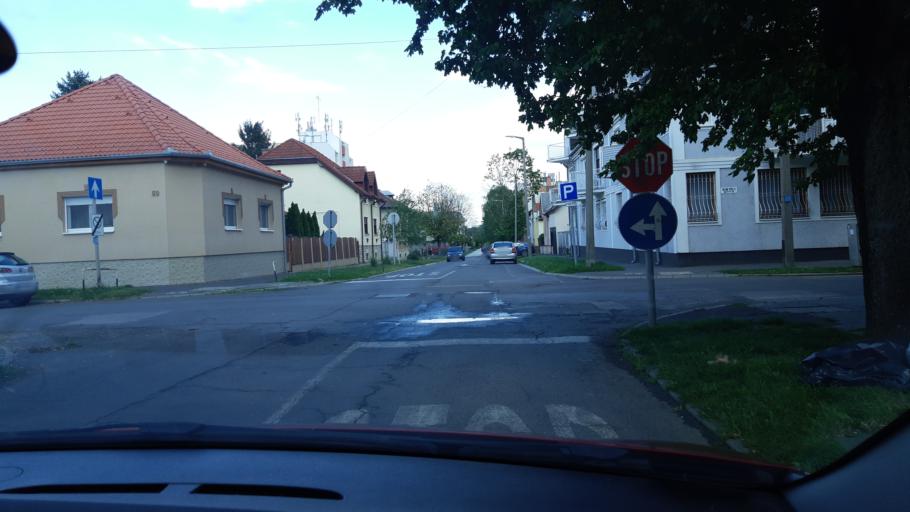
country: HU
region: Somogy
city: Kaposvar
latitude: 46.3620
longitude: 17.7969
